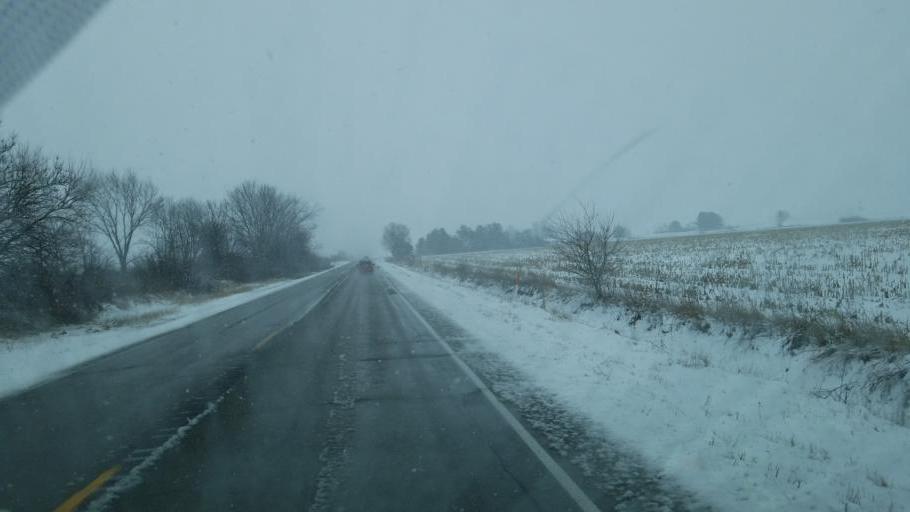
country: US
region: Indiana
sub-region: Wayne County
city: Hagerstown
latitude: 40.0358
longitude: -85.2047
